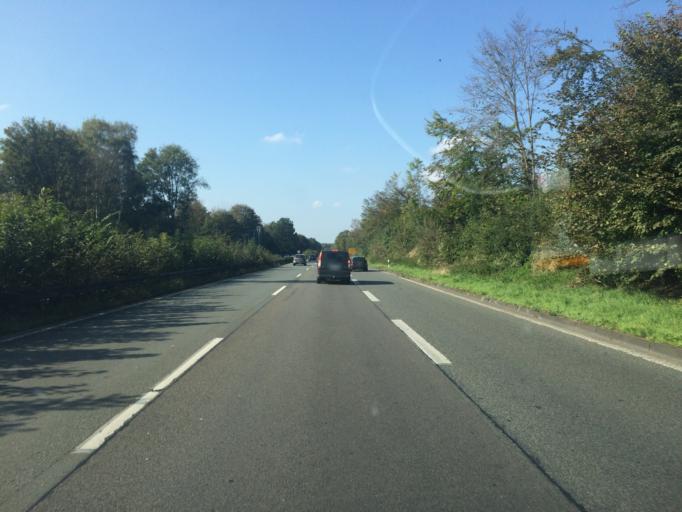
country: DE
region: North Rhine-Westphalia
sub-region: Regierungsbezirk Arnsberg
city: Holzwickede
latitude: 51.5069
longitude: 7.5719
